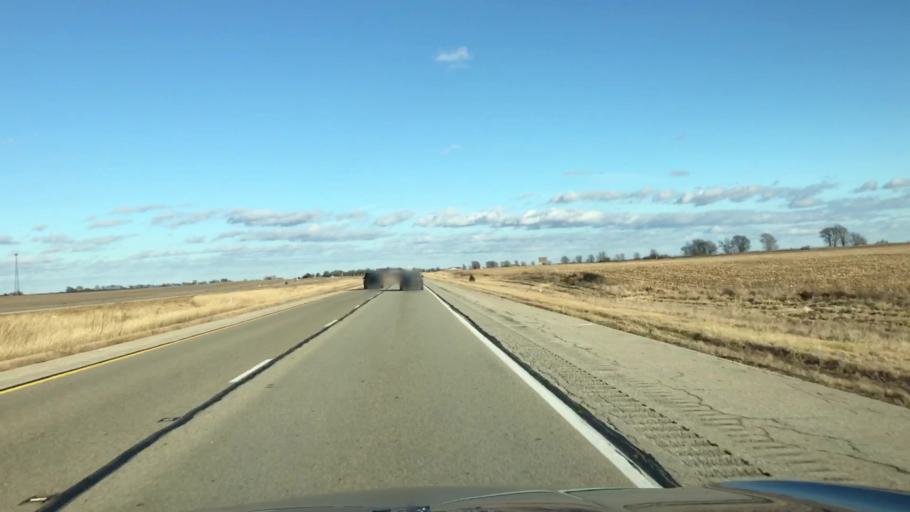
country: US
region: Illinois
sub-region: McLean County
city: Lexington
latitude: 40.5855
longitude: -88.8737
